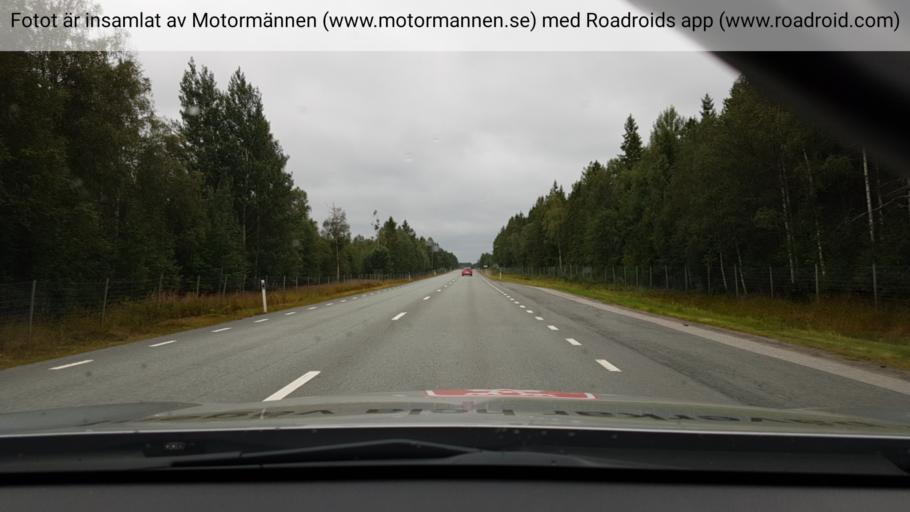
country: SE
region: Vaesterbotten
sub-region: Robertsfors Kommun
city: Robertsfors
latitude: 64.0574
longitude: 20.8479
